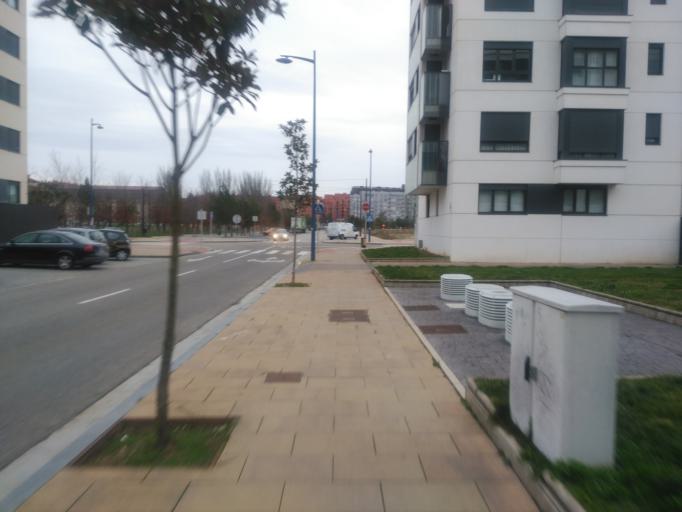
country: ES
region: Castille and Leon
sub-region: Provincia de Burgos
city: Burgos
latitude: 42.3352
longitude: -3.7095
